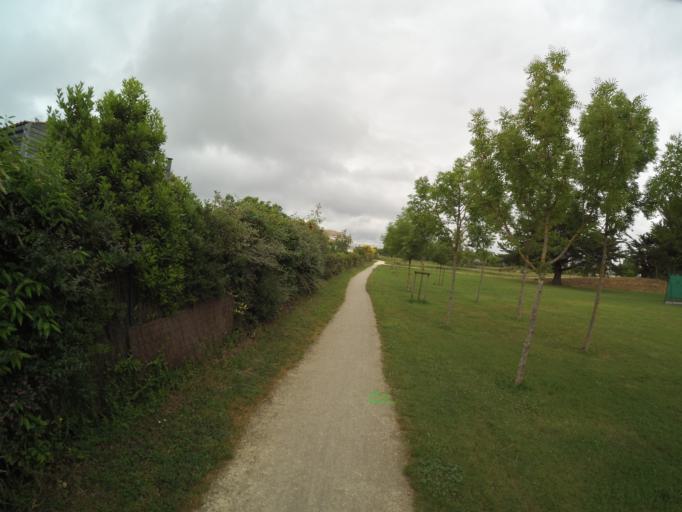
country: FR
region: Poitou-Charentes
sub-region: Departement de la Charente-Maritime
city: Aytre
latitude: 46.1290
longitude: -1.1277
